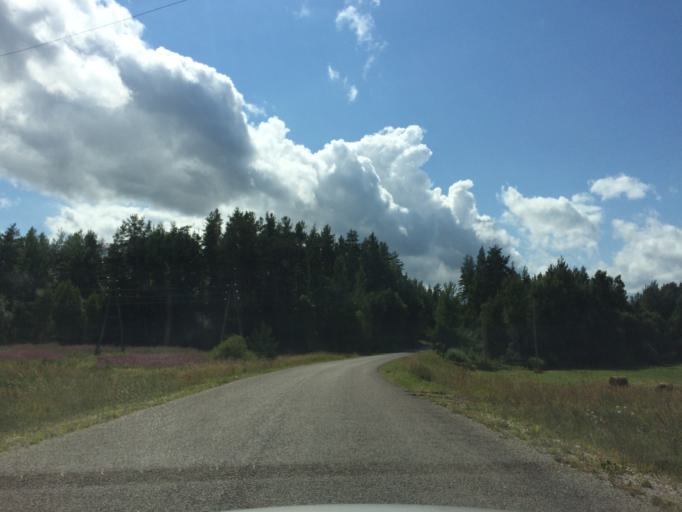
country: LV
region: Rezekne
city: Rezekne
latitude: 56.5515
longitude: 27.3692
